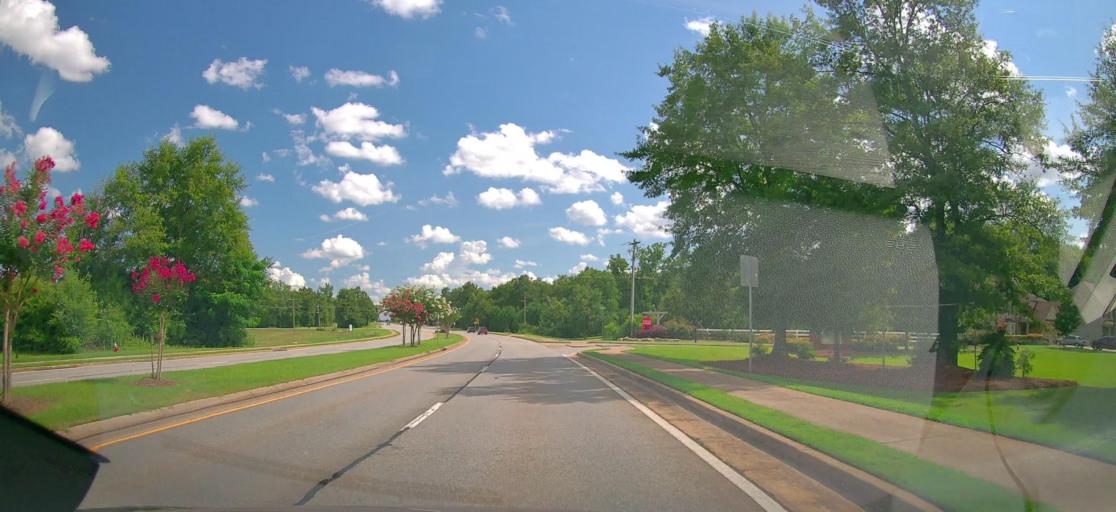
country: US
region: Georgia
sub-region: Houston County
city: Perry
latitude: 32.5313
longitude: -83.6621
